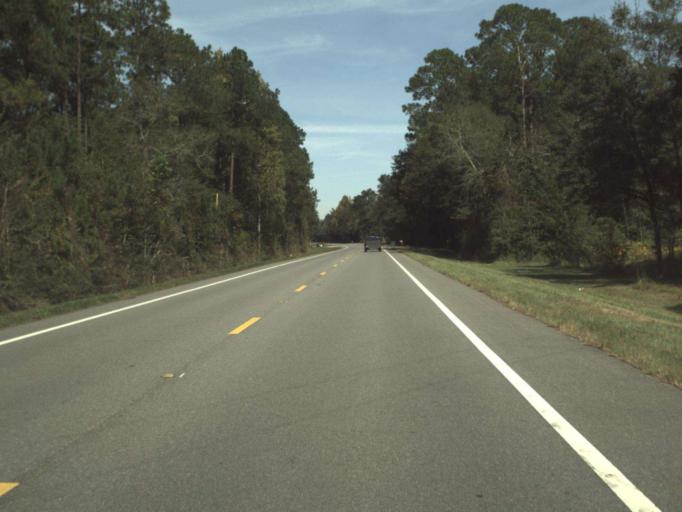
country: US
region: Florida
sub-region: Washington County
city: Chipley
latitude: 30.8159
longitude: -85.5335
